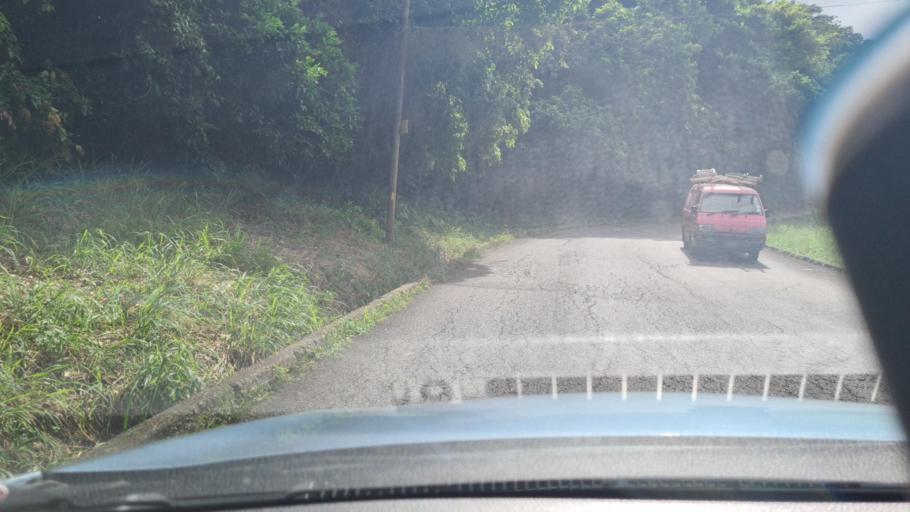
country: BB
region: Saint Joseph
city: Bathsheba
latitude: 13.2038
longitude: -59.5355
